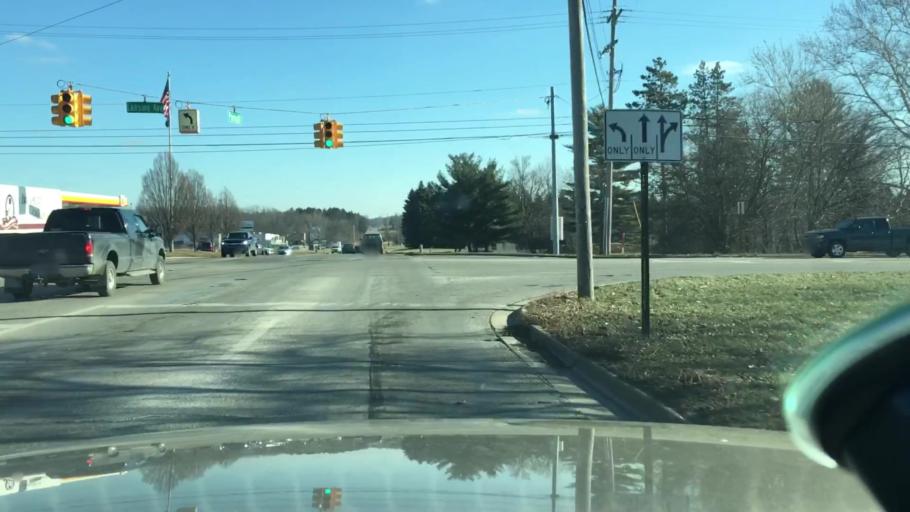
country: US
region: Michigan
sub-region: Jackson County
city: Jackson
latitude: 42.2911
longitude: -84.4139
